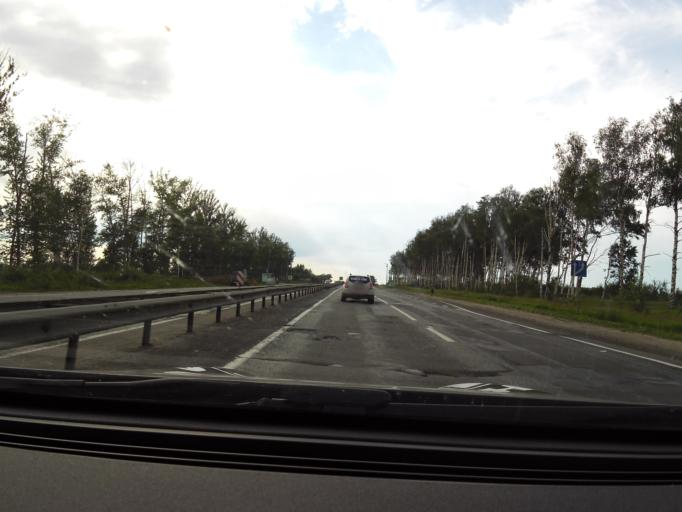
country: RU
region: Vladimir
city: Novovyazniki
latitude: 56.2121
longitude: 42.2631
